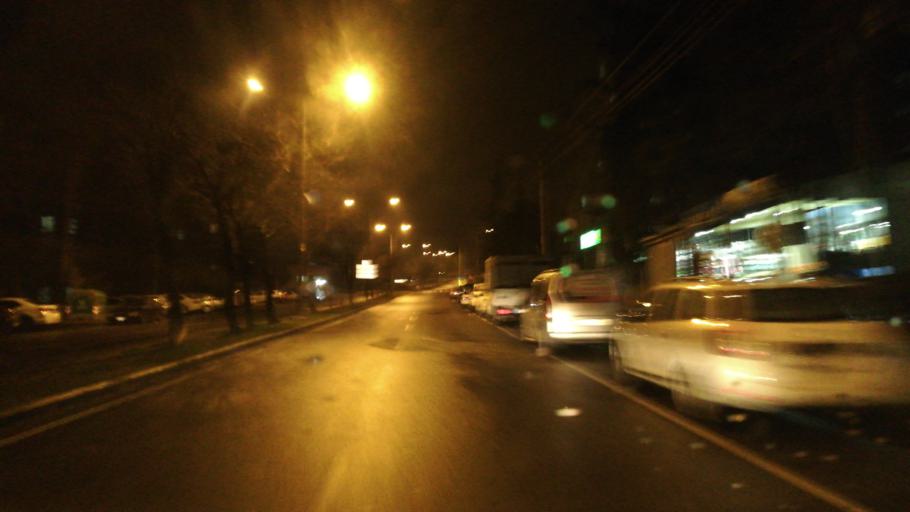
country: TR
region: Kahramanmaras
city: Kahramanmaras
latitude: 37.5942
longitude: 36.8685
